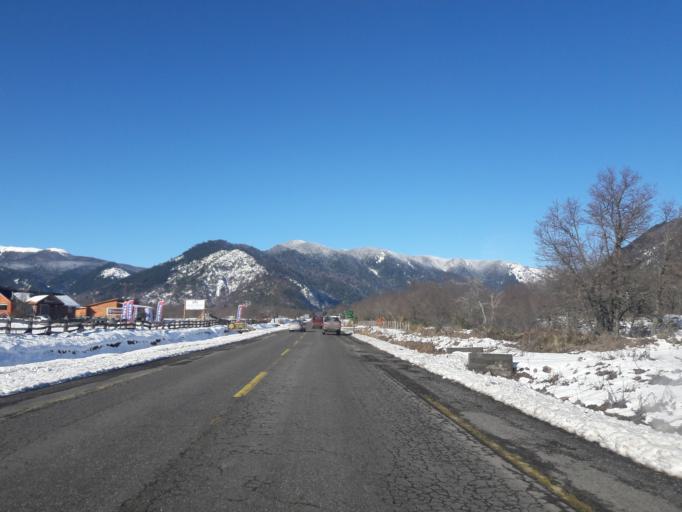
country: CL
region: Araucania
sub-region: Provincia de Cautin
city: Vilcun
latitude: -38.4742
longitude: -71.5544
